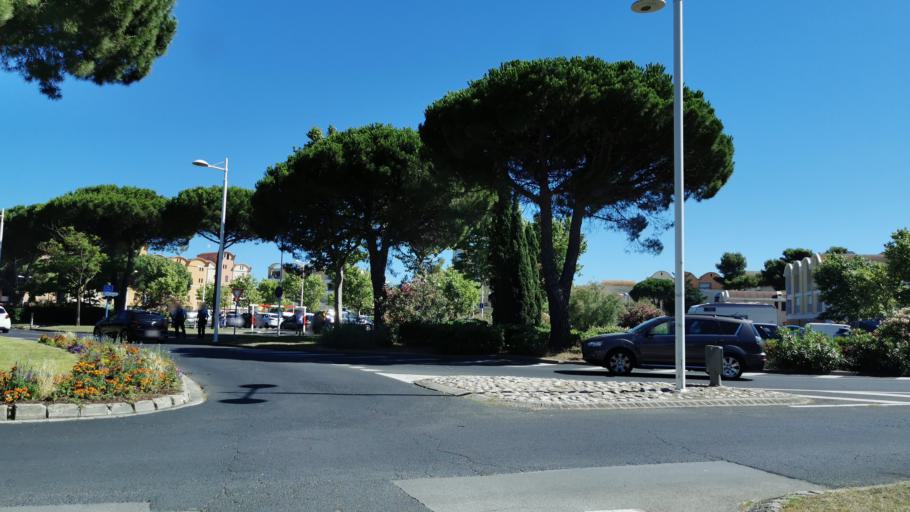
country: FR
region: Languedoc-Roussillon
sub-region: Departement de l'Aude
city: Gruissan
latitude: 43.1123
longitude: 3.0934
